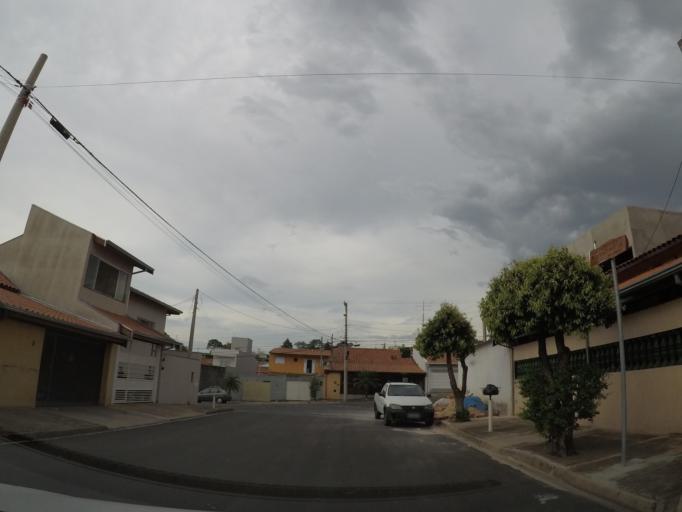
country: BR
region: Sao Paulo
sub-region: Sumare
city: Sumare
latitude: -22.8162
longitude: -47.2513
